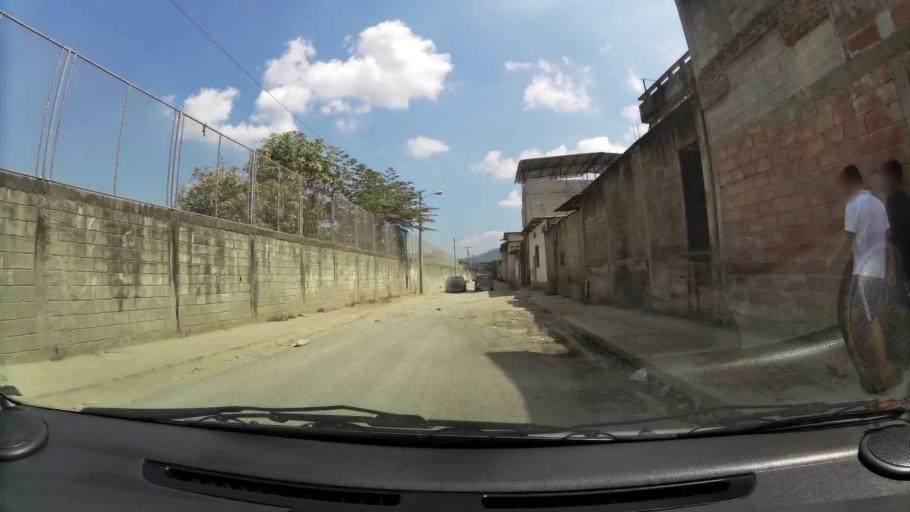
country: EC
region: Guayas
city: Guayaquil
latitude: -2.1261
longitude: -79.9293
